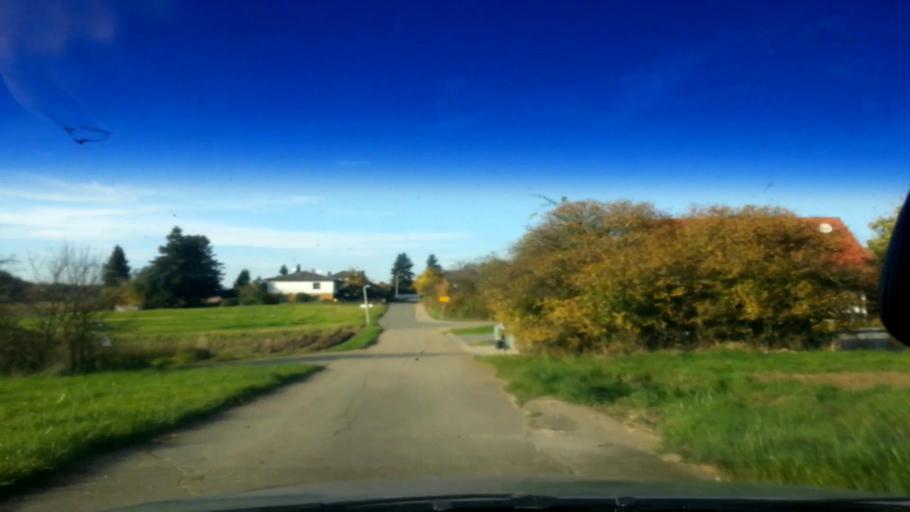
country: DE
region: Bavaria
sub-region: Upper Franconia
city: Memmelsdorf
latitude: 49.9284
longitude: 10.9804
